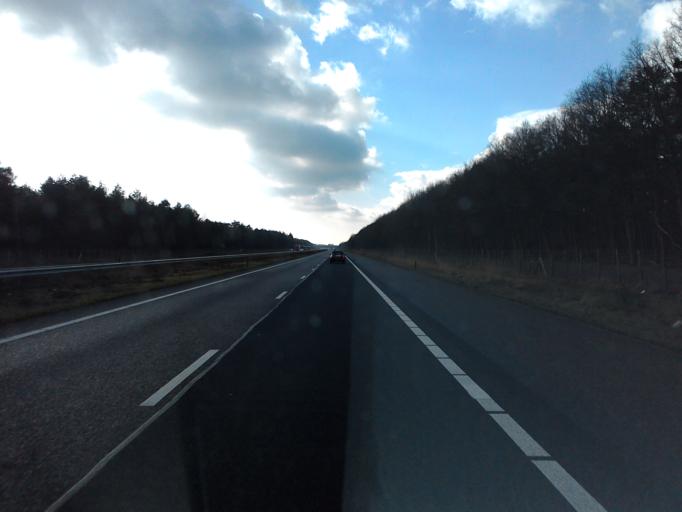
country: NL
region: North Brabant
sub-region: Gemeente Bladel en Netersel
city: Bladel
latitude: 51.3406
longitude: 5.2559
